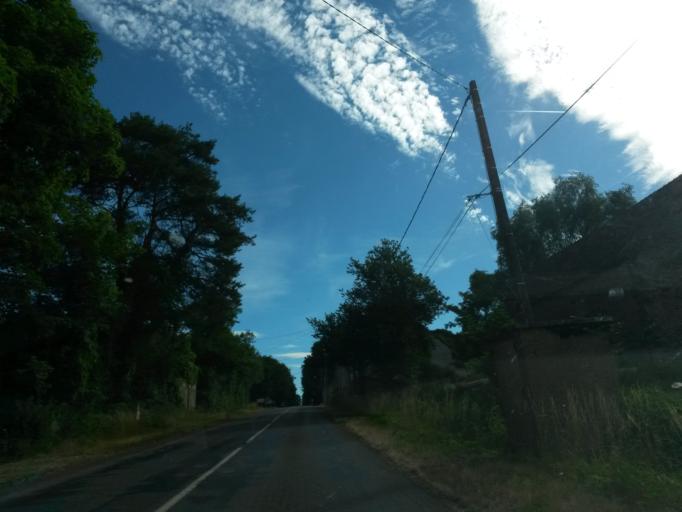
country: FR
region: Bourgogne
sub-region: Departement de la Nievre
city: Varzy
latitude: 47.3054
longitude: 3.2839
